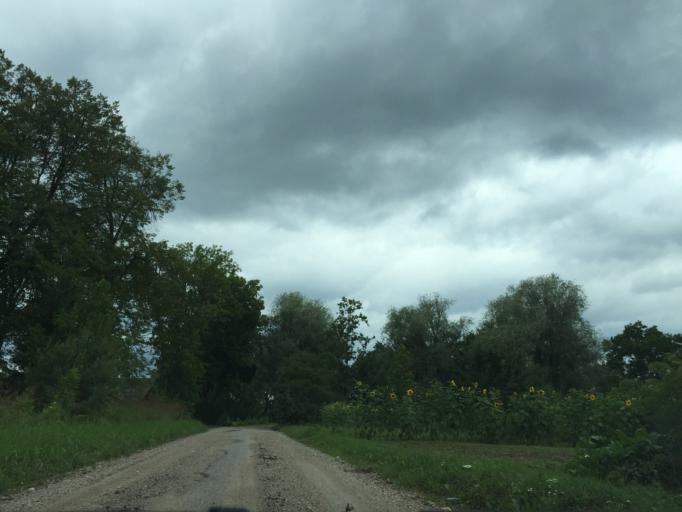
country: LV
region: Seja
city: Loja
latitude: 57.1466
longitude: 24.6617
